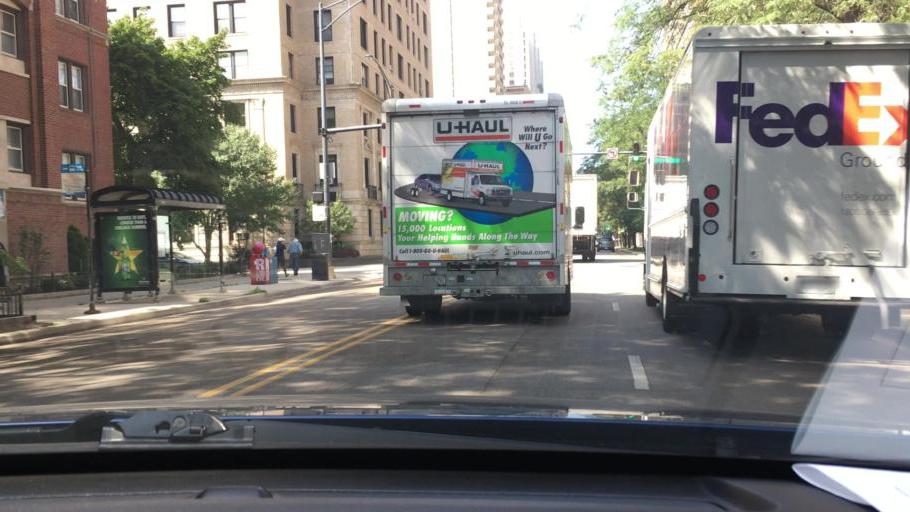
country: US
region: Illinois
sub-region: Cook County
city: Chicago
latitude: 41.9373
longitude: -87.6394
